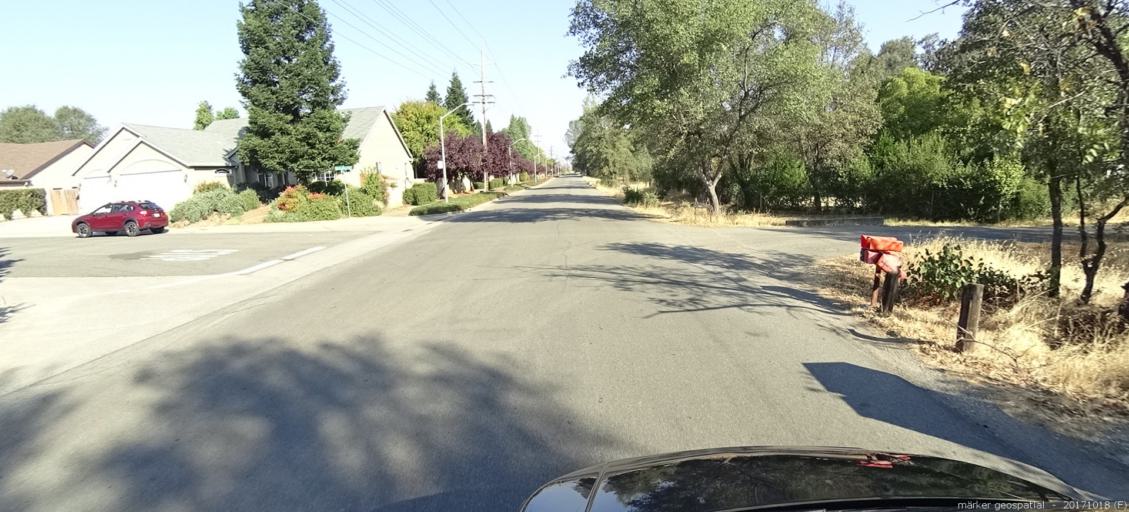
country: US
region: California
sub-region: Shasta County
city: Palo Cedro
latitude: 40.5417
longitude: -122.3146
